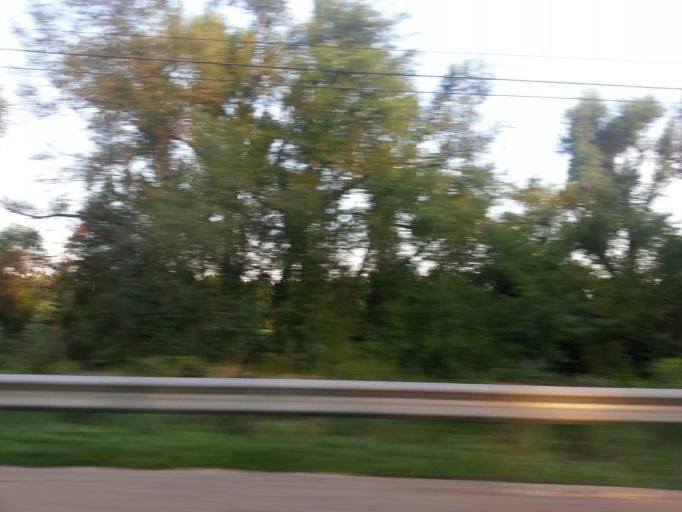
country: US
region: Tennessee
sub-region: Monroe County
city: Sweetwater
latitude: 35.6272
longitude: -84.4453
